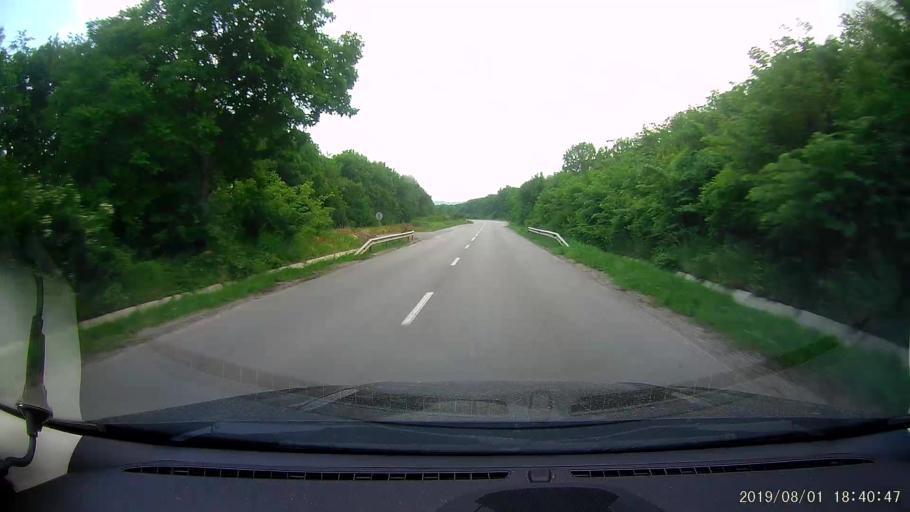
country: BG
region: Shumen
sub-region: Obshtina Khitrino
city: Gara Khitrino
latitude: 43.3588
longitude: 26.9208
